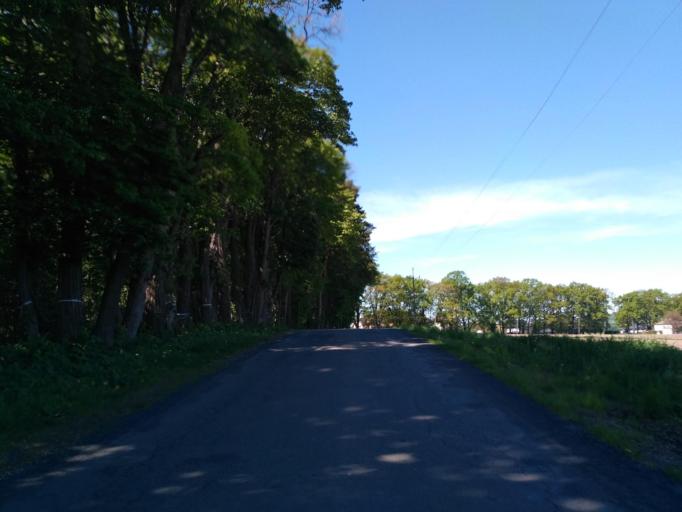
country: PL
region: Subcarpathian Voivodeship
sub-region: Powiat brzozowski
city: Turze Pole
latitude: 49.6461
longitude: 22.0020
